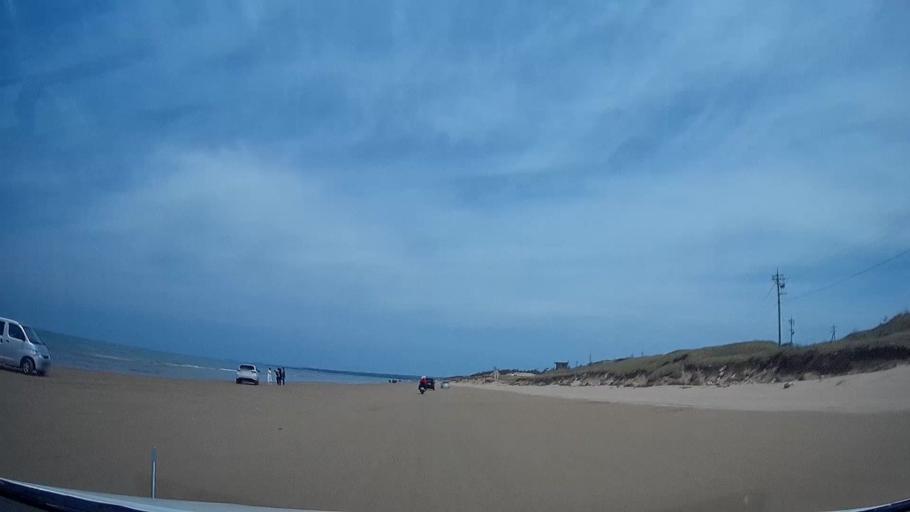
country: JP
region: Ishikawa
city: Hakui
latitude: 36.8548
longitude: 136.7548
